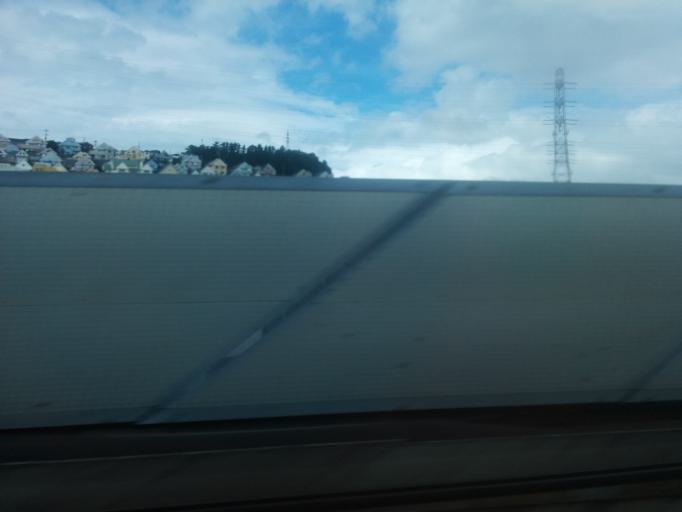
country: JP
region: Kanagawa
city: Oiso
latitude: 35.3392
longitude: 139.3045
